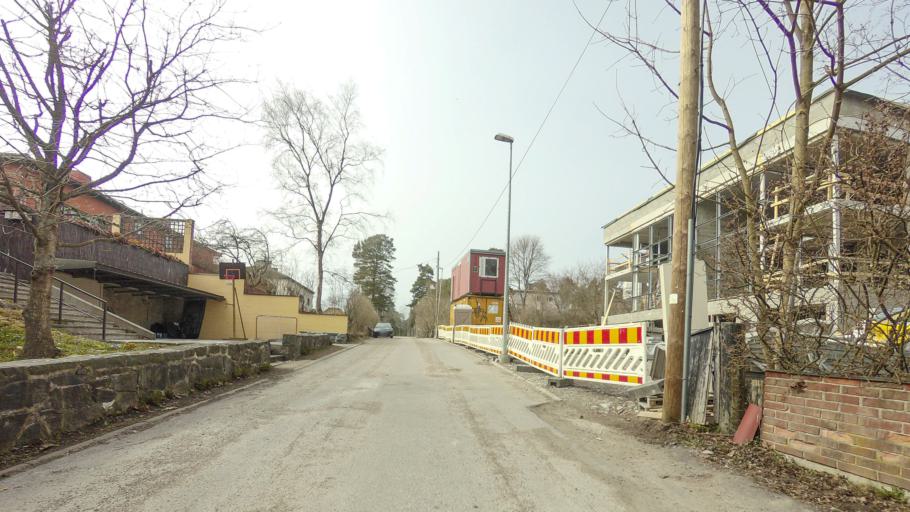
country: FI
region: Uusimaa
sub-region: Helsinki
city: Helsinki
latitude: 60.1832
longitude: 25.0036
